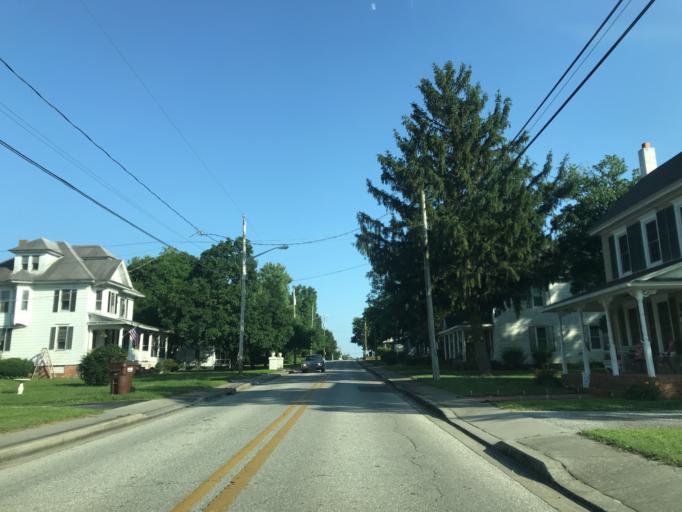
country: US
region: Maryland
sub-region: Wicomico County
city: Hebron
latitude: 38.5371
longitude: -75.7176
